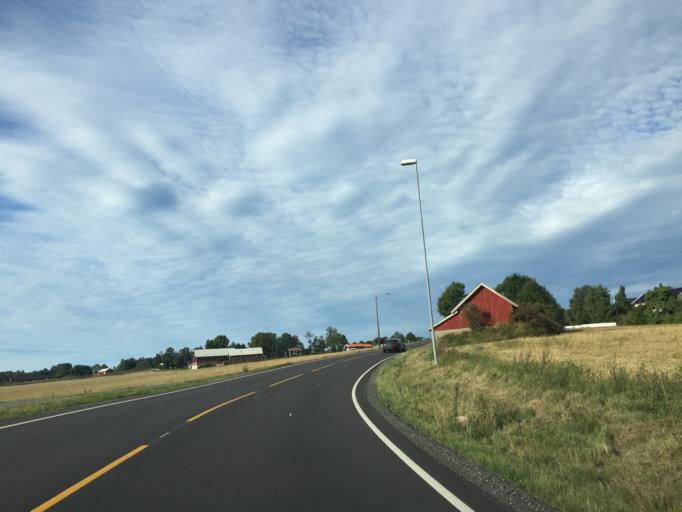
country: NO
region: Akershus
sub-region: Ski
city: Ski
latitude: 59.7195
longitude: 10.7824
